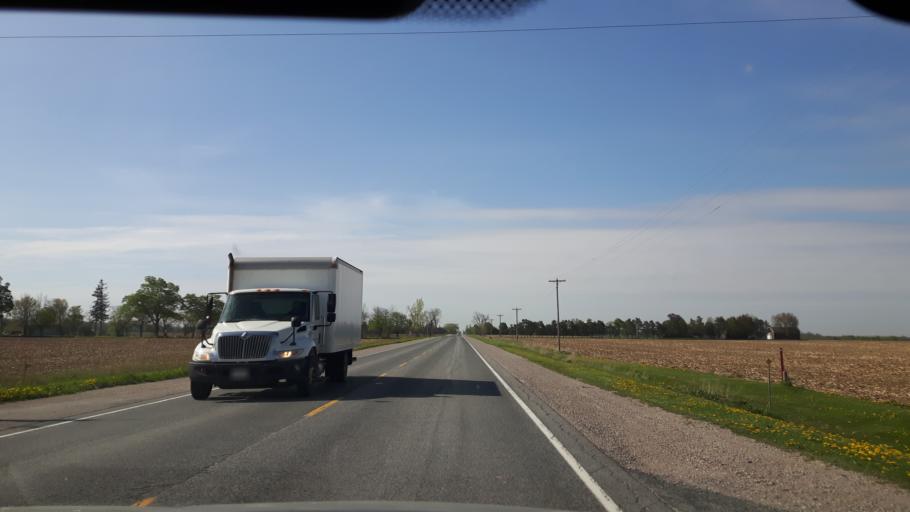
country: CA
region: Ontario
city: Bluewater
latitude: 43.4874
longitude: -81.5094
